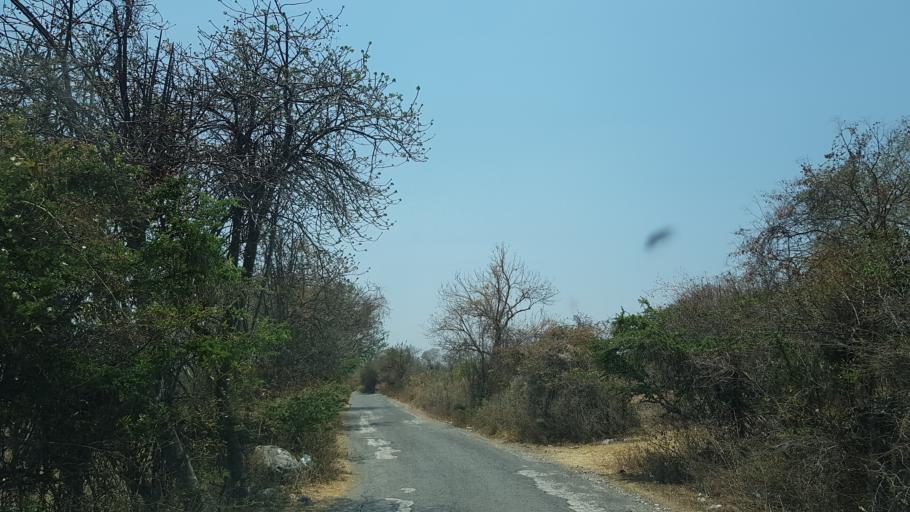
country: MX
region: Puebla
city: Huaquechula
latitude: 18.7880
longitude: -98.5443
